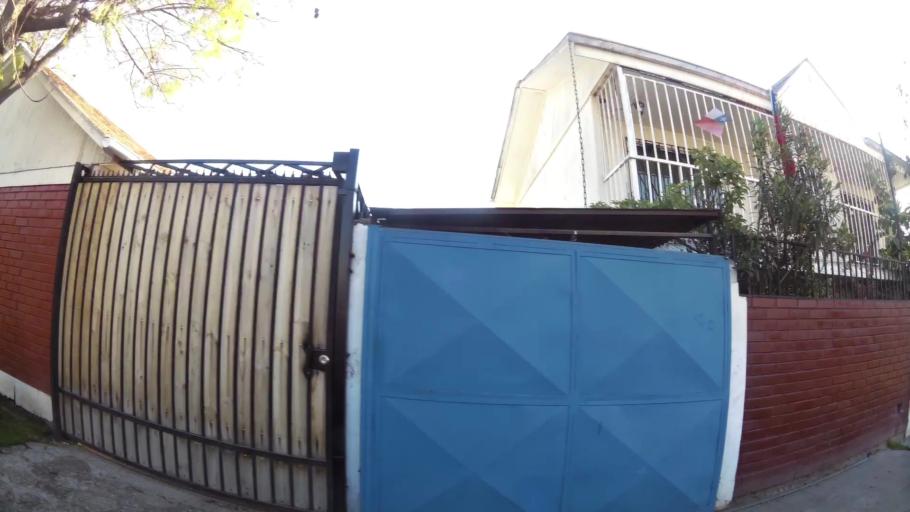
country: CL
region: Santiago Metropolitan
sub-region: Provincia de Santiago
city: La Pintana
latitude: -33.5544
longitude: -70.6253
